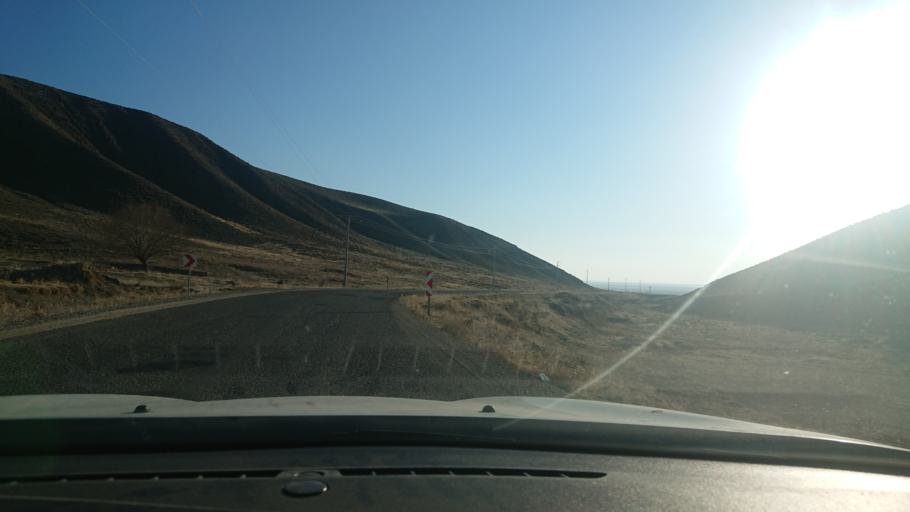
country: TR
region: Aksaray
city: Acipinar
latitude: 38.6882
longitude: 33.7429
